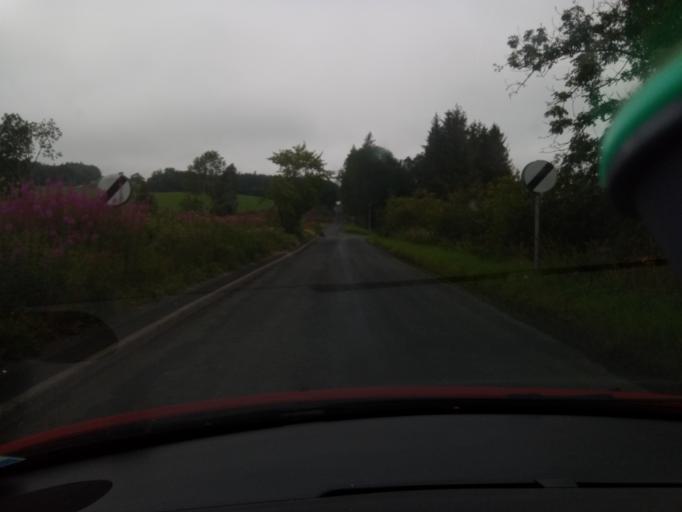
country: GB
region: Scotland
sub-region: Fife
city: Pathhead
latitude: 55.7351
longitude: -2.9110
